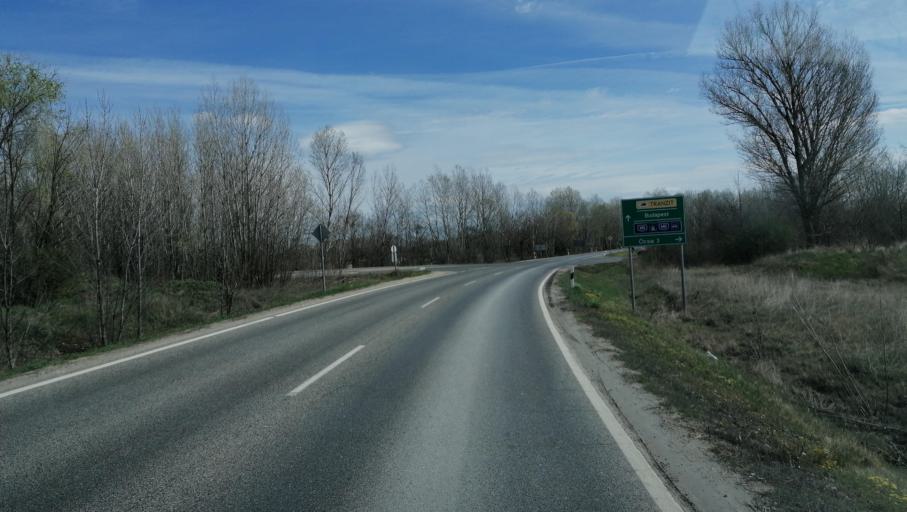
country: HU
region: Pest
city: Alsonemedi
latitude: 47.3036
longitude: 19.1826
